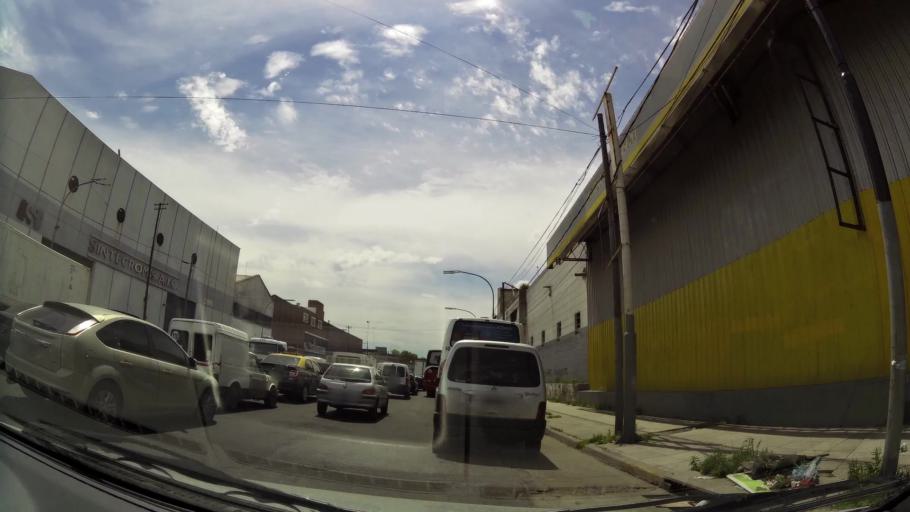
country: AR
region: Buenos Aires
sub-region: Partido de Lanus
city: Lanus
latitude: -34.6665
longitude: -58.4174
